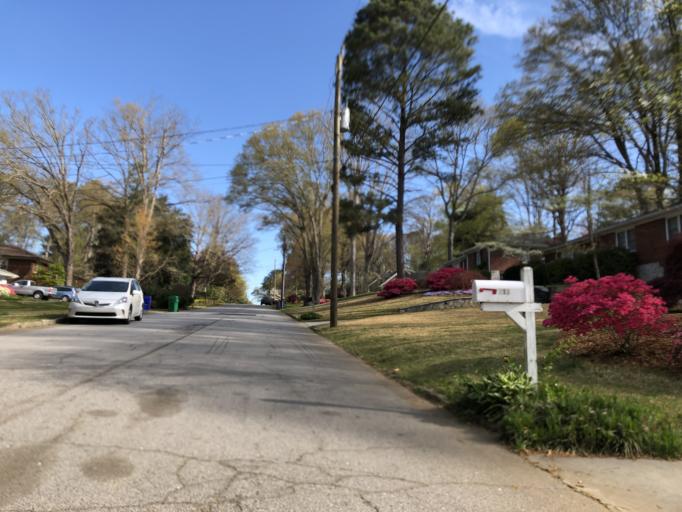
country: US
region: Georgia
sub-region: DeKalb County
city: North Decatur
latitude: 33.7977
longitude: -84.3002
